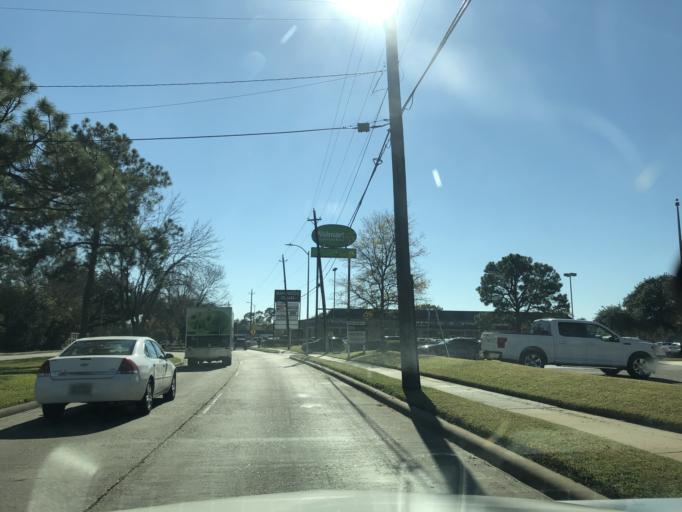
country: US
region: Texas
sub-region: Harris County
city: Bellaire
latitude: 29.6757
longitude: -95.4938
